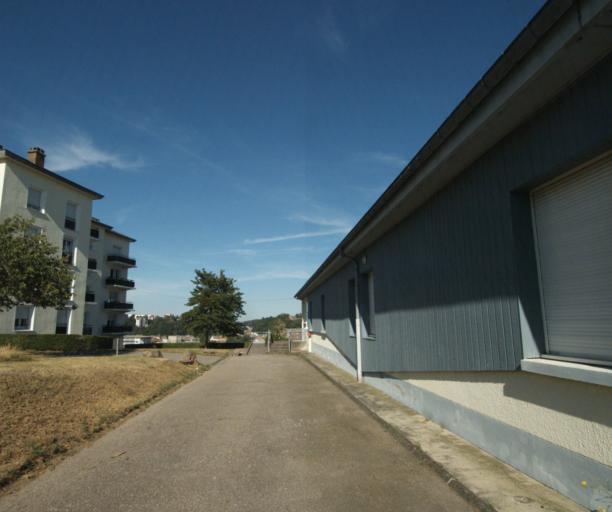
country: FR
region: Lorraine
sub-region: Departement des Vosges
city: Chantraine
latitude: 48.1708
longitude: 6.4402
